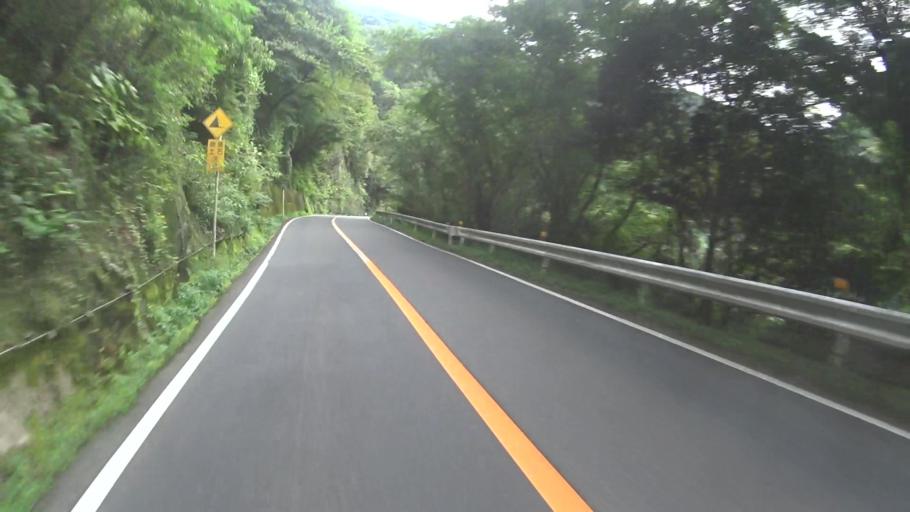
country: JP
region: Kyoto
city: Uji
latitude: 34.8947
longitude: 135.8685
